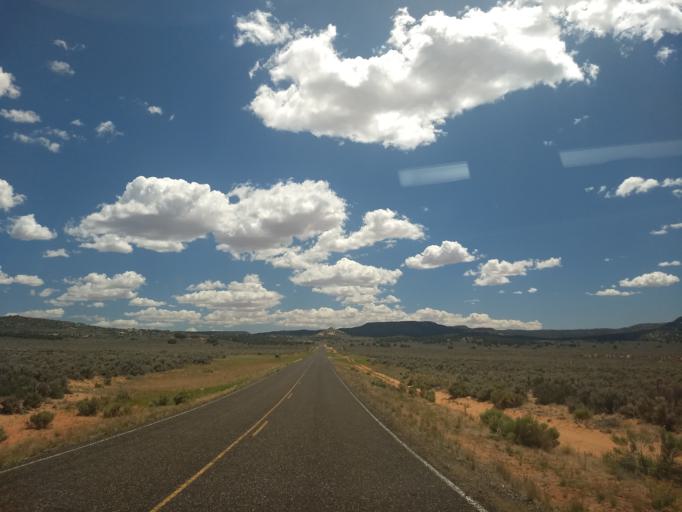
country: US
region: Utah
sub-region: Kane County
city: Kanab
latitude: 37.1632
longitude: -112.6658
